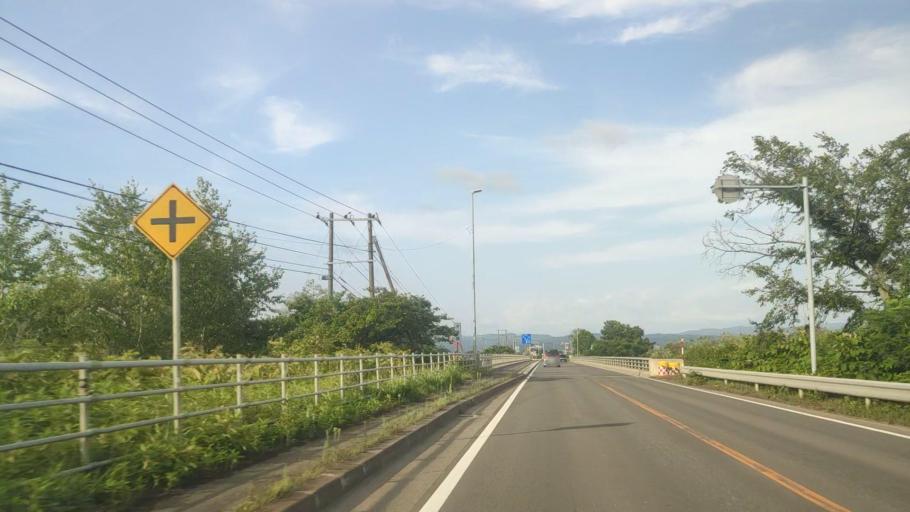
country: JP
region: Hokkaido
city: Iwamizawa
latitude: 43.0239
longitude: 141.8077
